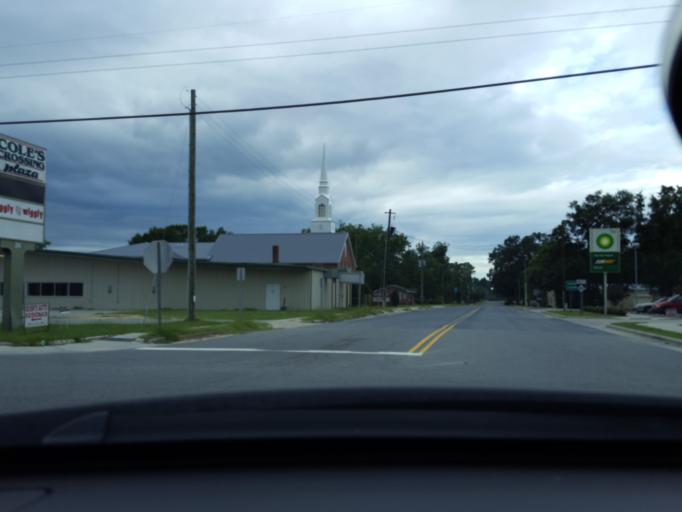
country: US
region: North Carolina
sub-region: Sampson County
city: Roseboro
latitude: 34.7858
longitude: -78.3940
